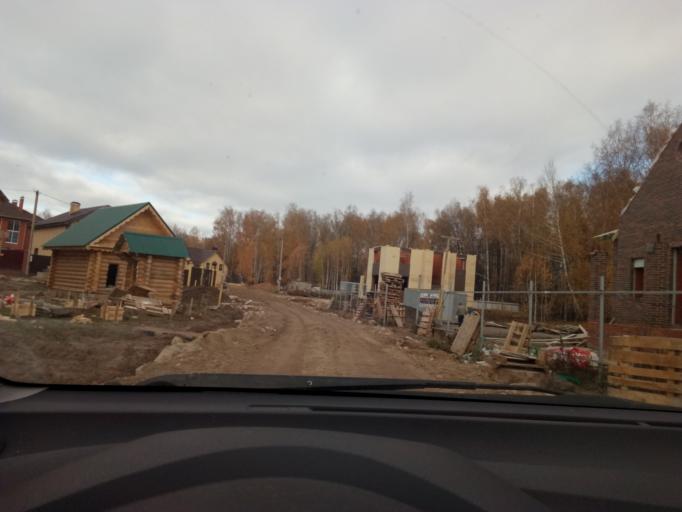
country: RU
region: Tatarstan
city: Staroye Arakchino
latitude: 55.9695
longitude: 49.0452
